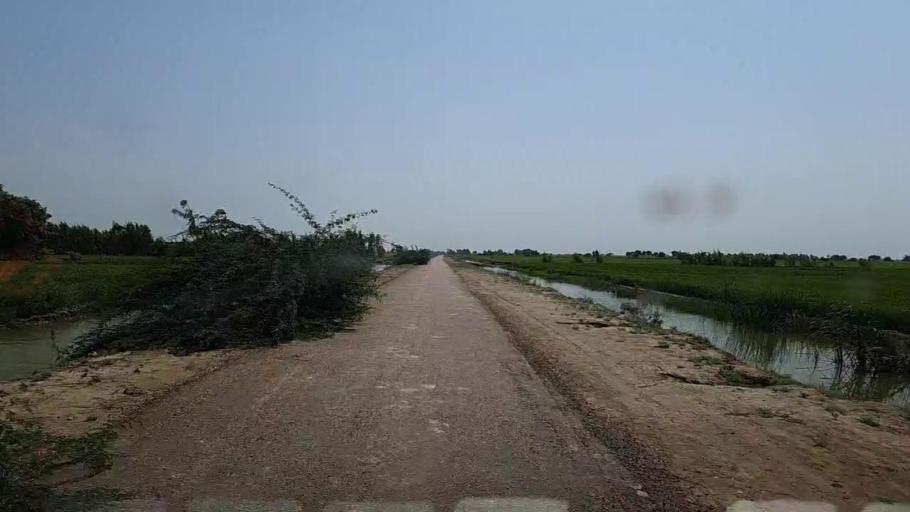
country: PK
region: Sindh
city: Mirpur Batoro
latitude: 24.6110
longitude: 68.4523
